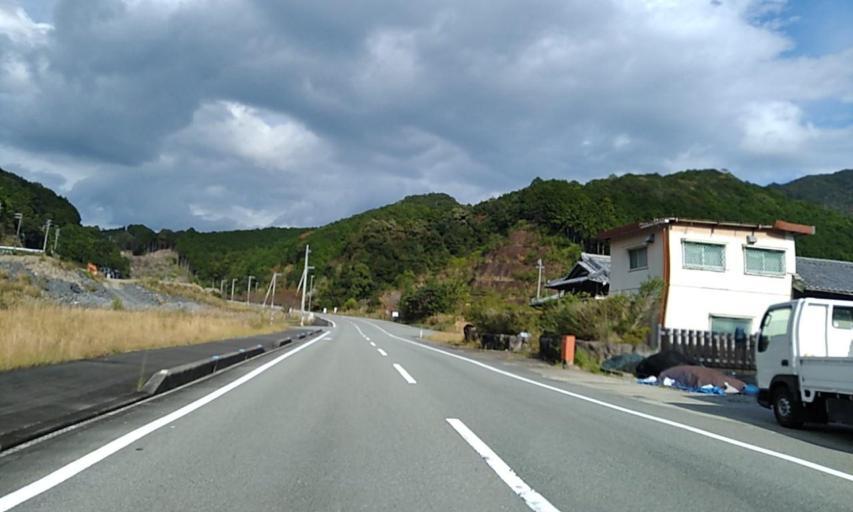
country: JP
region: Mie
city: Owase
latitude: 34.2296
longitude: 136.3948
